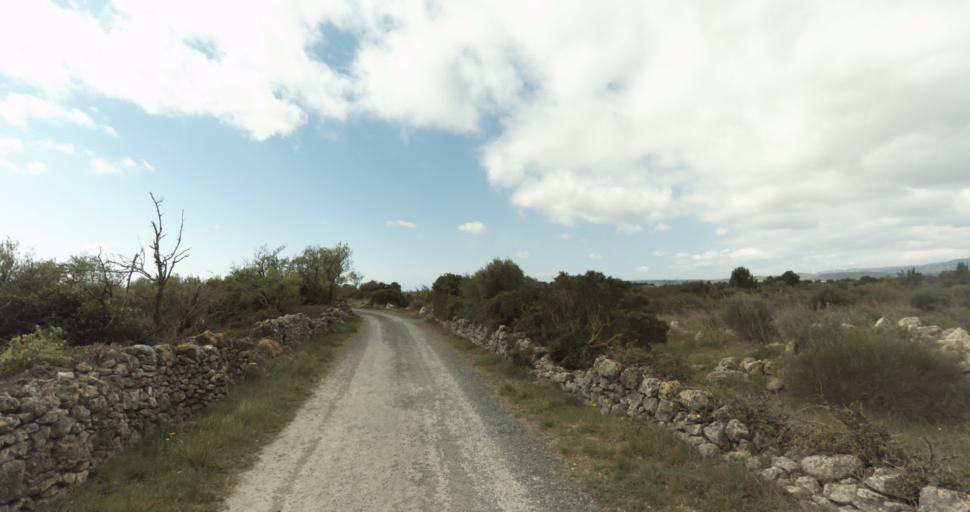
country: FR
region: Languedoc-Roussillon
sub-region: Departement de l'Aude
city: Leucate
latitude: 42.9145
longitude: 3.0357
